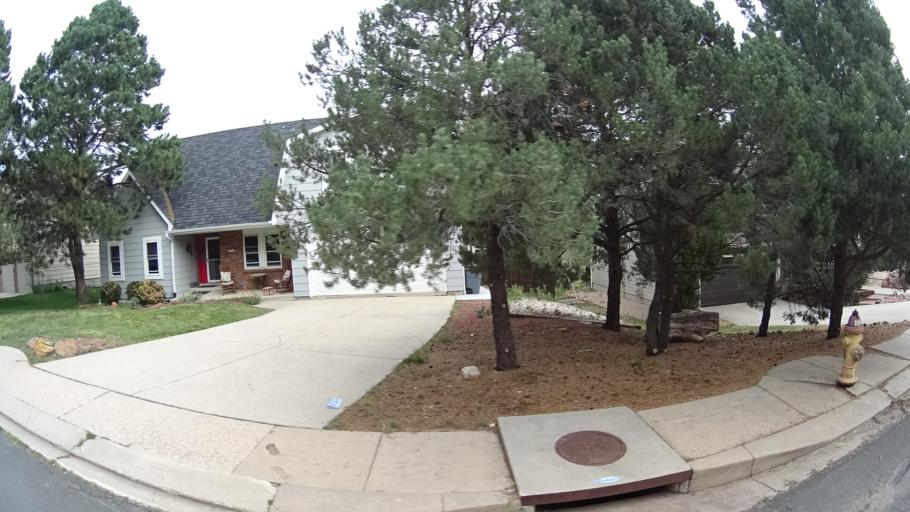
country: US
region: Colorado
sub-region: El Paso County
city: Air Force Academy
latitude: 38.9286
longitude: -104.8427
